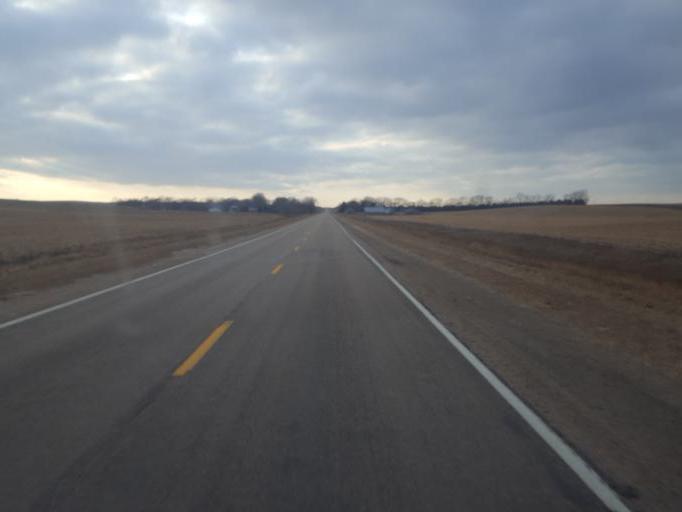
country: US
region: Nebraska
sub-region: Knox County
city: Bloomfield
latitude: 42.6128
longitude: -97.4553
